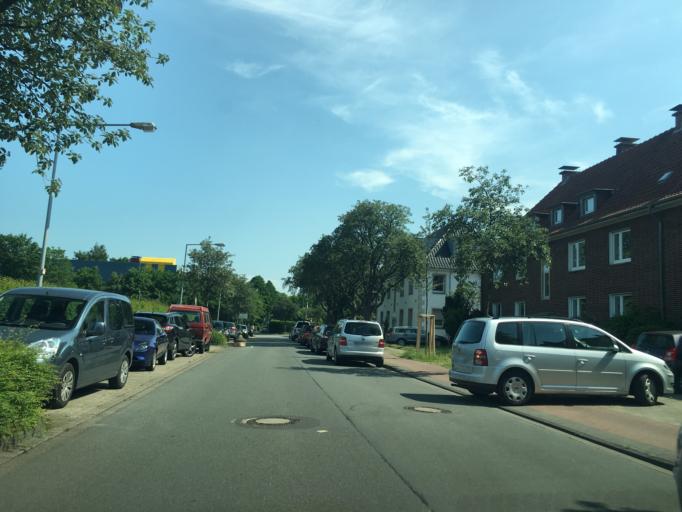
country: DE
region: North Rhine-Westphalia
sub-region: Regierungsbezirk Munster
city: Muenster
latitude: 51.9699
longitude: 7.6487
